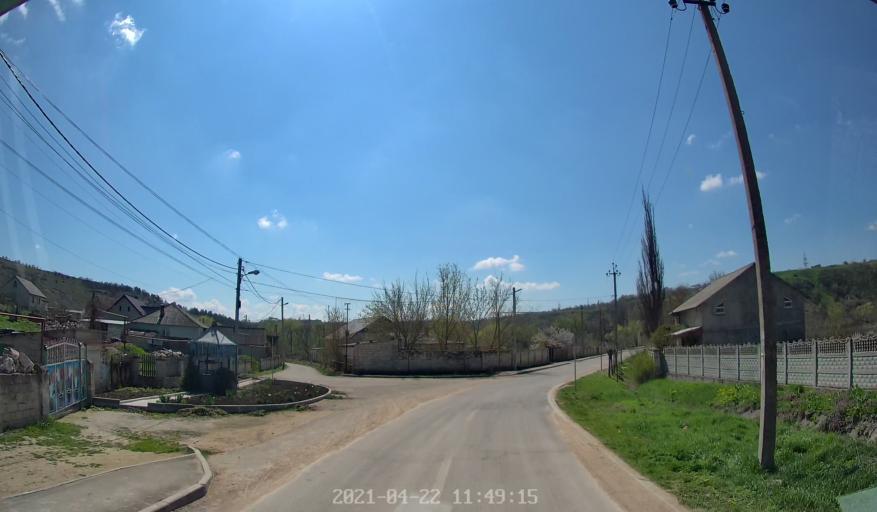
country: MD
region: Chisinau
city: Ciorescu
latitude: 47.1433
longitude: 28.8977
